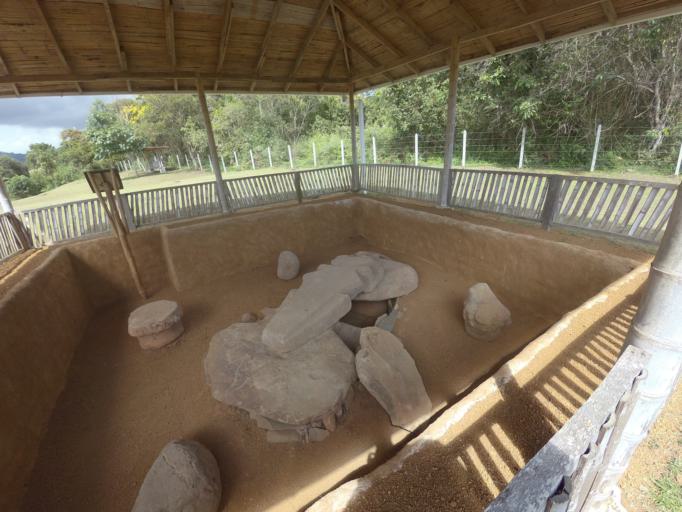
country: CO
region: Huila
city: Isnos
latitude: 1.9151
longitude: -76.2387
